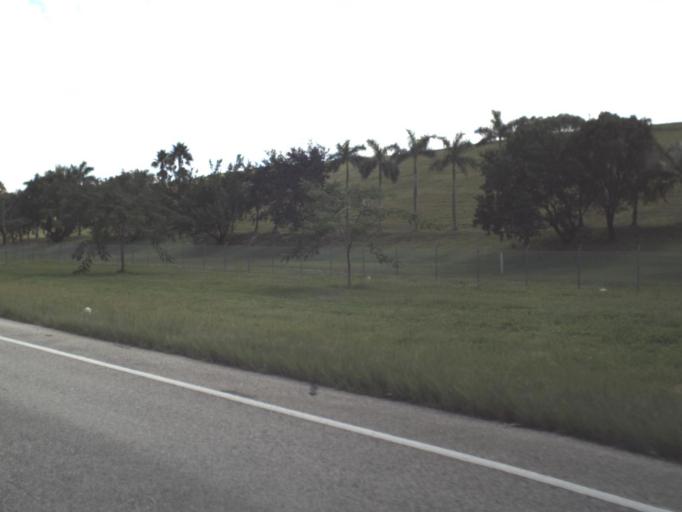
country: US
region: Florida
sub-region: Miami-Dade County
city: Country Club
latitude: 25.9709
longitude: -80.2923
